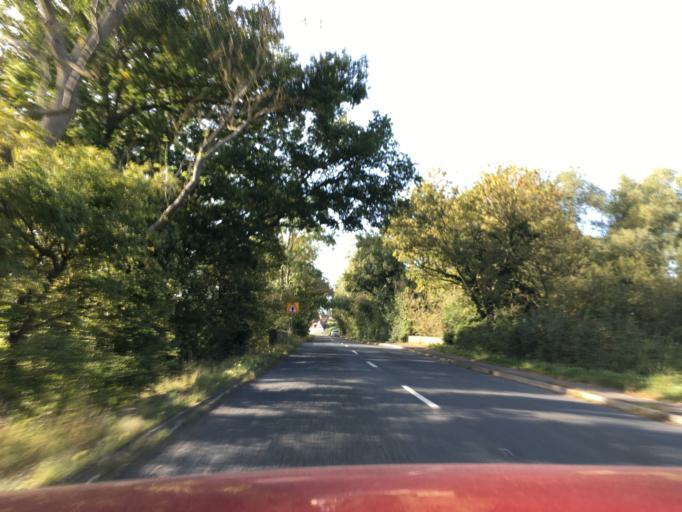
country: GB
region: England
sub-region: Gloucestershire
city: Tewkesbury
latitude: 51.9518
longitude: -2.2337
